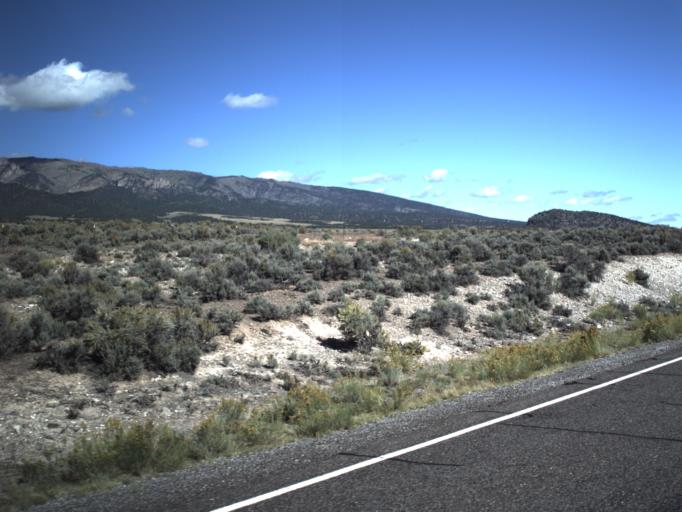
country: US
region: Utah
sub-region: Piute County
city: Junction
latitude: 38.3204
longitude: -111.9639
